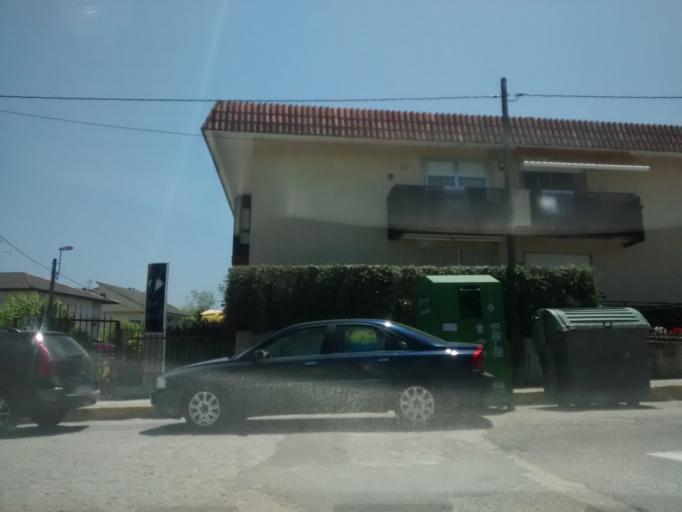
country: ES
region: Galicia
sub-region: Provincia de Pontevedra
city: Nigran
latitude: 42.1244
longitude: -8.8204
